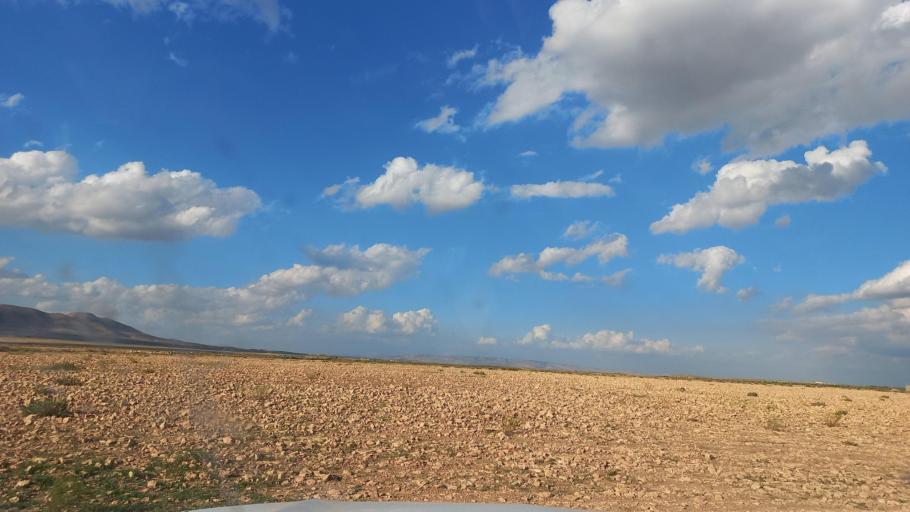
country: TN
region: Al Qasrayn
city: Sbiba
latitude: 35.3859
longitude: 9.0717
